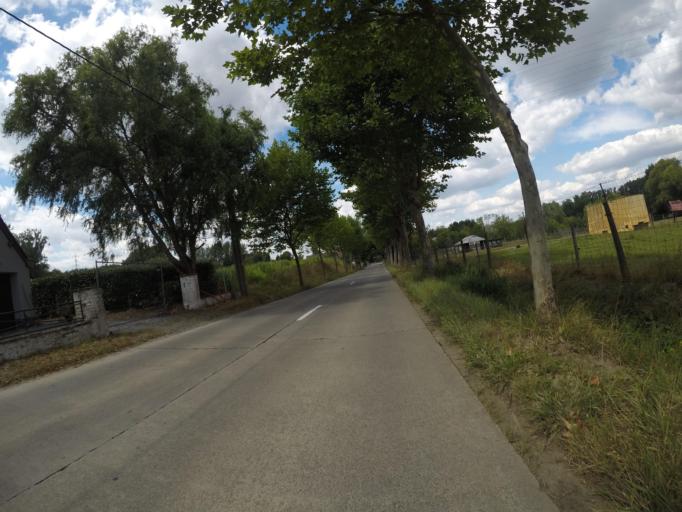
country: BE
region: Flanders
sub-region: Provincie Vlaams-Brabant
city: Ternat
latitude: 50.8586
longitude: 4.1483
